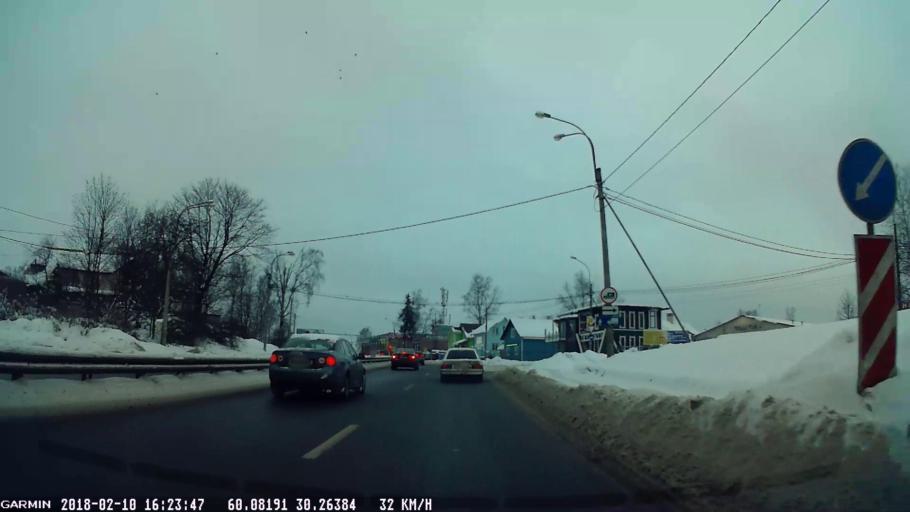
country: RU
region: St.-Petersburg
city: Pargolovo
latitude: 60.0821
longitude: 30.2634
